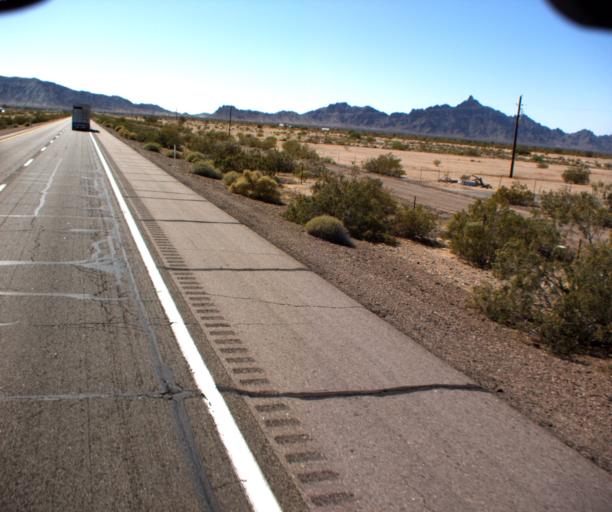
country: US
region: Arizona
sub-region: Yuma County
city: Wellton
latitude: 32.7401
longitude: -113.6904
